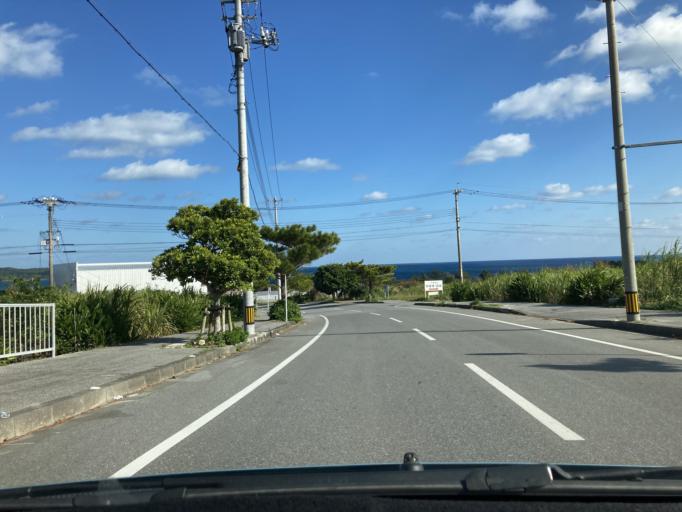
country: JP
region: Okinawa
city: Katsuren-haebaru
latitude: 26.3048
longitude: 127.9183
